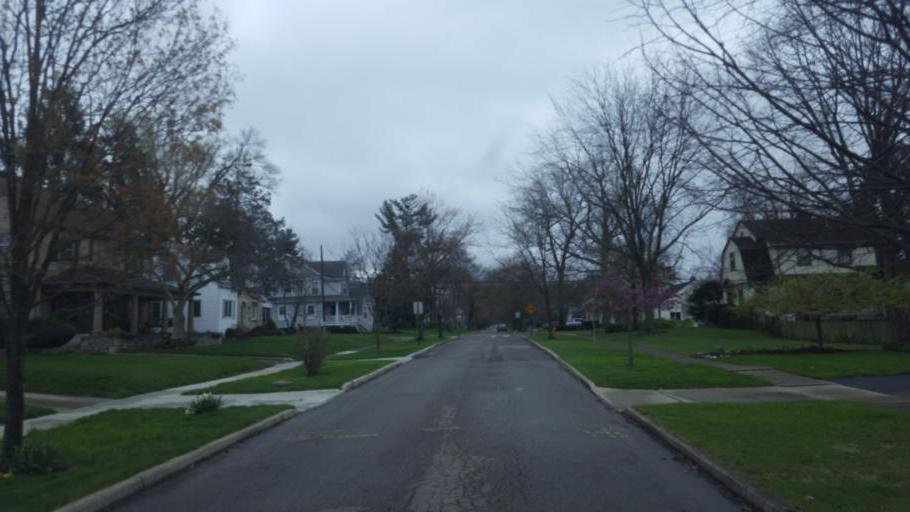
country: US
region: Ohio
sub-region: Franklin County
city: Worthington
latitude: 40.0408
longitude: -83.0112
